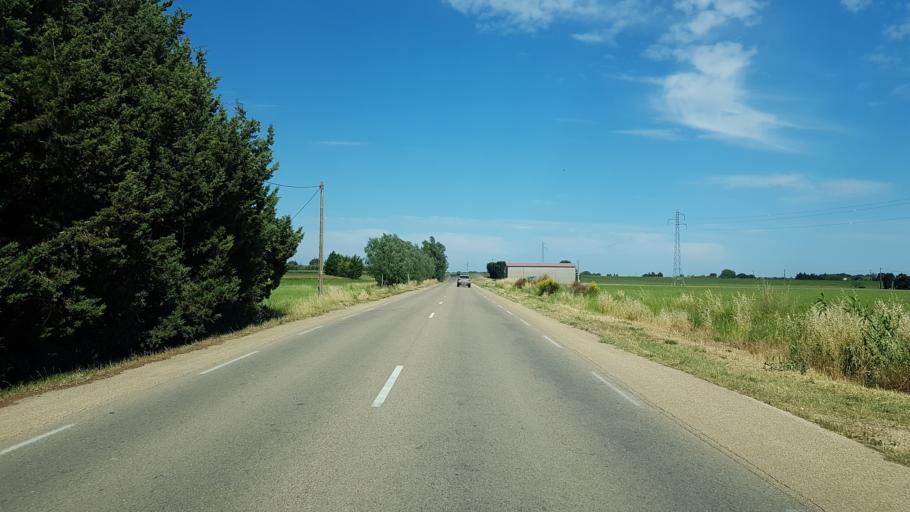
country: FR
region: Provence-Alpes-Cote d'Azur
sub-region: Departement des Bouches-du-Rhone
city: Fontvieille
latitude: 43.6635
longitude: 4.6992
